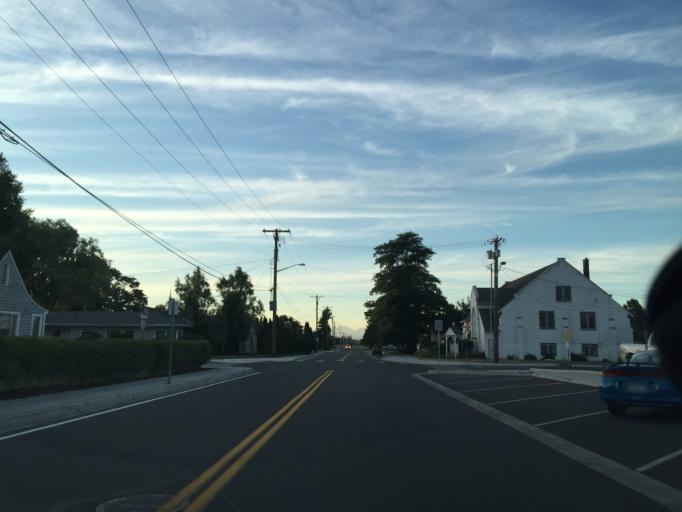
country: US
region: Washington
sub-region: Whatcom County
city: Everson
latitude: 48.9205
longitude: -122.3425
